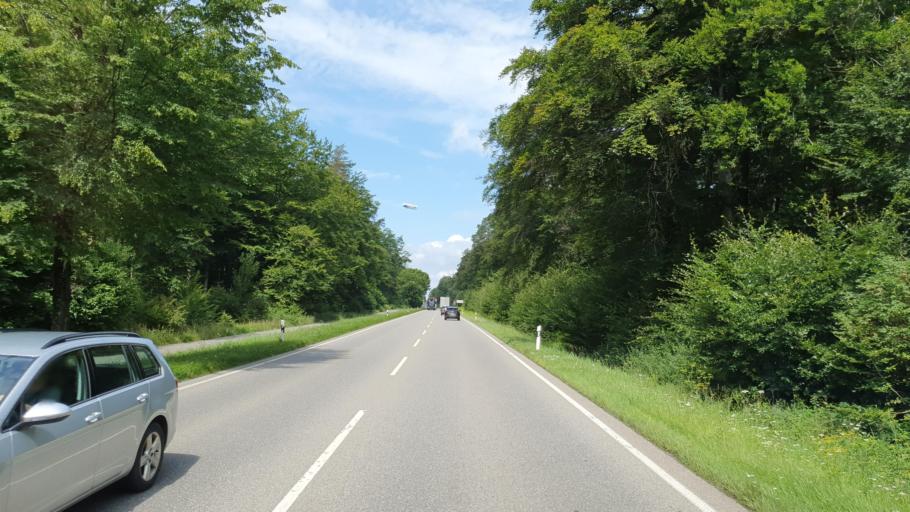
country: DE
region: Baden-Wuerttemberg
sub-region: Tuebingen Region
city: Eriskirch
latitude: 47.6212
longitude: 9.5596
